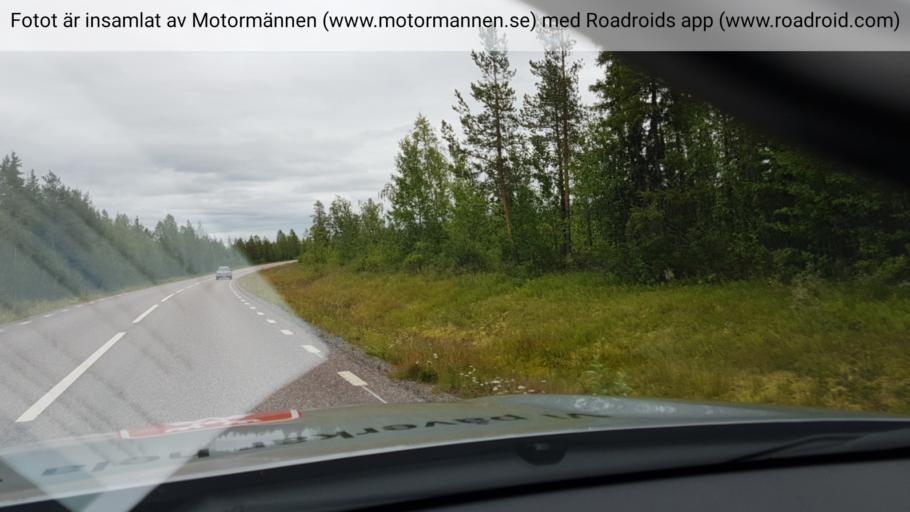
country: SE
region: Norrbotten
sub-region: Gallivare Kommun
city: Gaellivare
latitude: 67.0310
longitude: 21.7602
